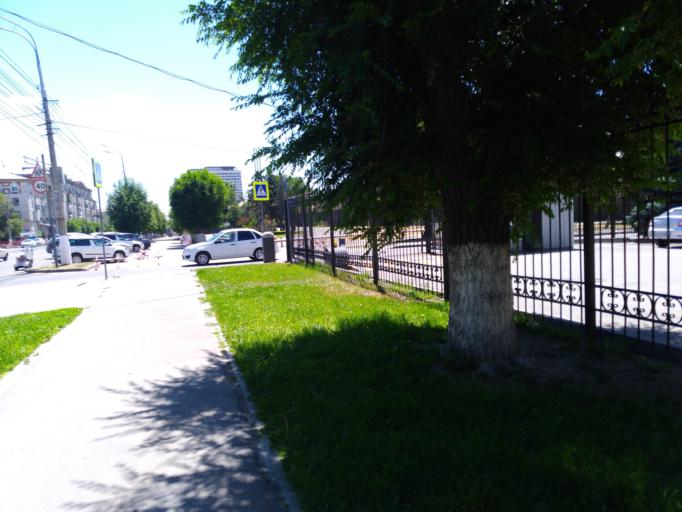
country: RU
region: Volgograd
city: Volgograd
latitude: 48.7080
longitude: 44.5059
